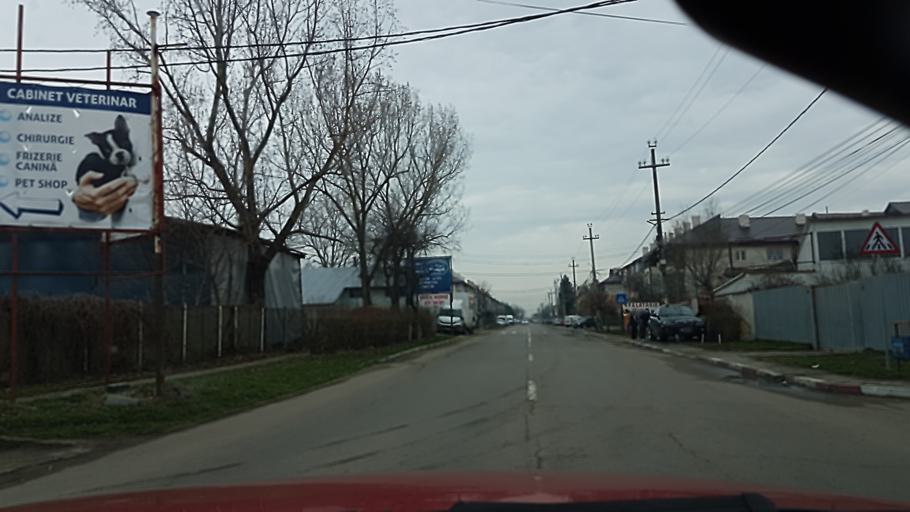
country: RO
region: Ilfov
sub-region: Comuna Corbeanca
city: Corbeanca
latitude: 44.6135
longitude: 26.0794
